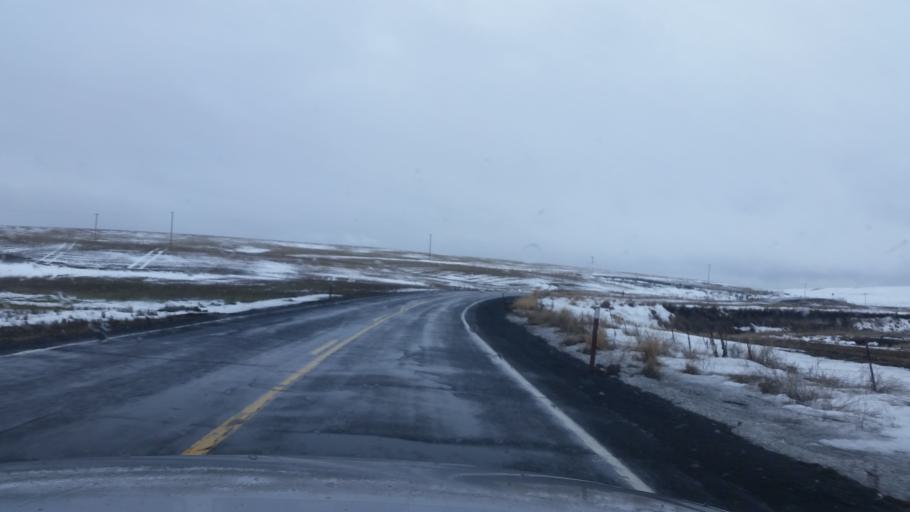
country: US
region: Washington
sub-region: Lincoln County
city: Davenport
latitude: 47.3927
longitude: -118.1471
